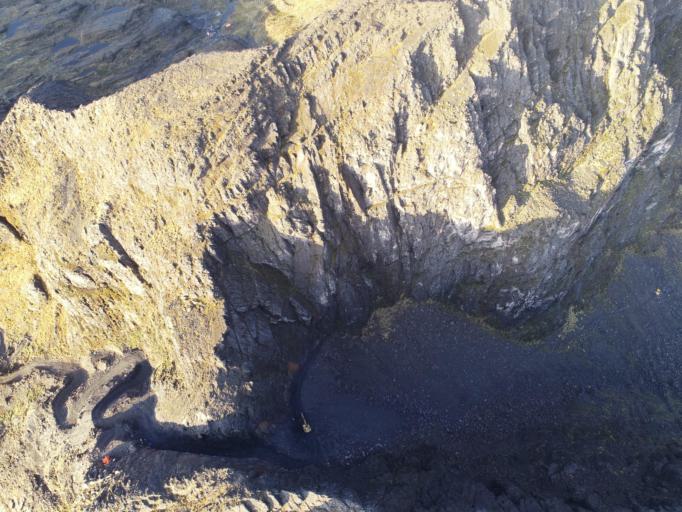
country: PE
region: Puno
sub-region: San Antonio De Putina
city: Sina
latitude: -14.7356
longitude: -69.0501
